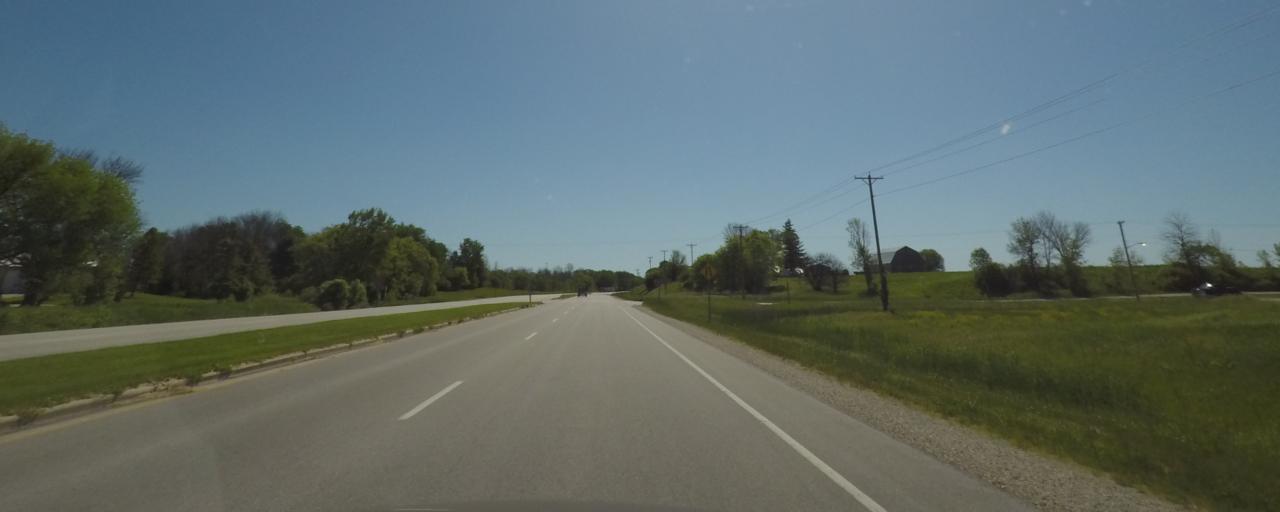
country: US
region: Wisconsin
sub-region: Sheboygan County
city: Plymouth
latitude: 43.7471
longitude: -87.9397
